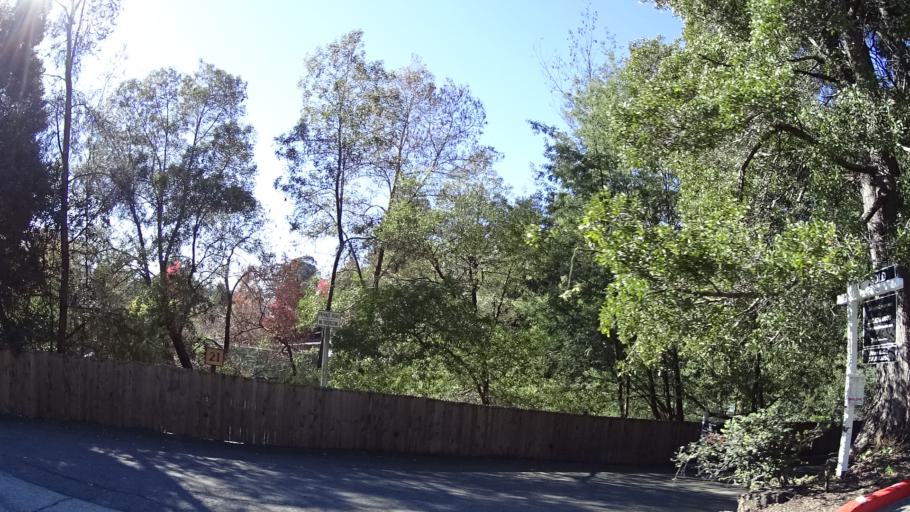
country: US
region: California
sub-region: Alameda County
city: Piedmont
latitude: 37.8205
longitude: -122.2177
